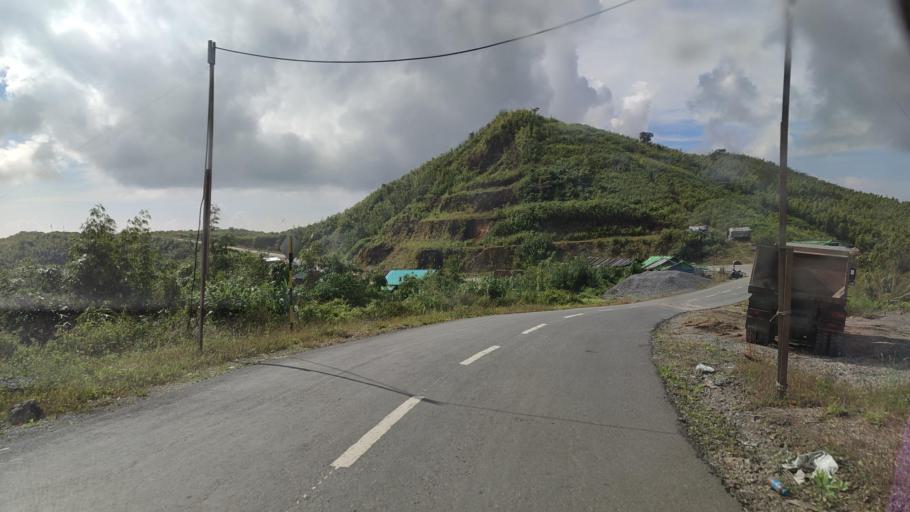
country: MM
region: Magway
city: Minbu
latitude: 19.8341
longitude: 94.2869
